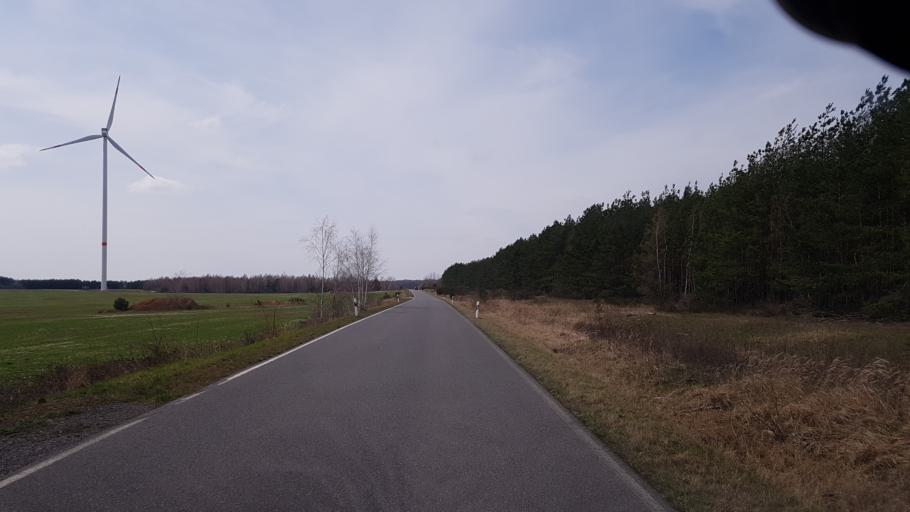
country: DE
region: Brandenburg
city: Schipkau
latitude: 51.5345
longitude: 13.8711
